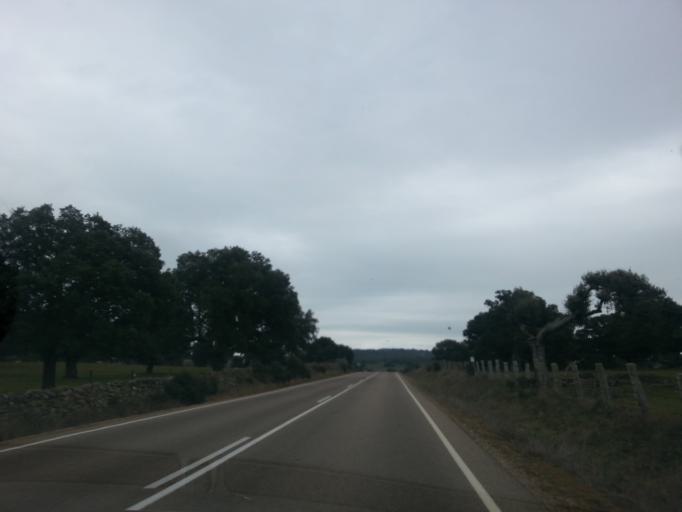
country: ES
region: Castille and Leon
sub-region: Provincia de Salamanca
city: Berrocal de Huebra
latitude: 40.7203
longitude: -5.9729
